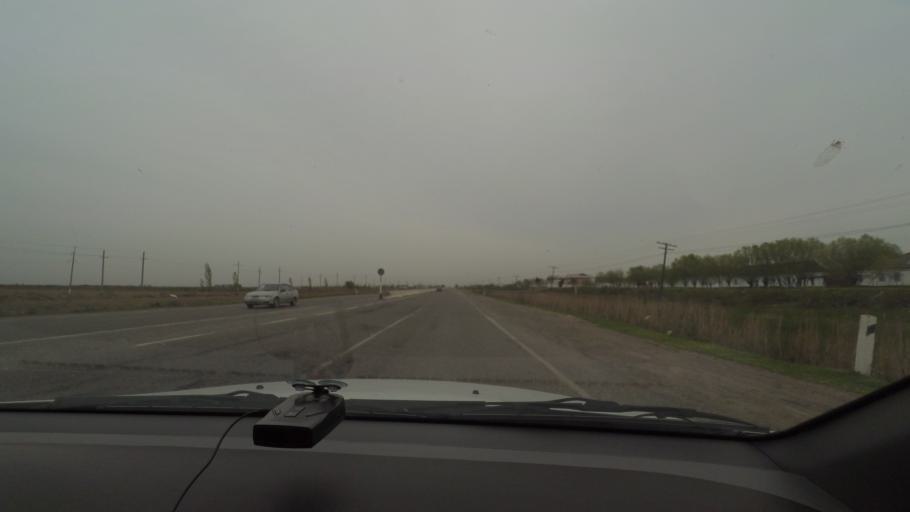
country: UZ
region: Sirdaryo
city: Guliston
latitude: 40.4955
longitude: 68.6352
